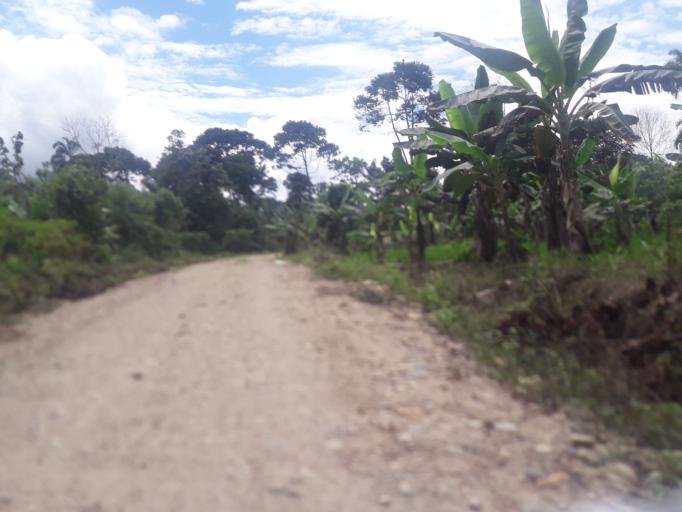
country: EC
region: Napo
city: Tena
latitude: -0.9756
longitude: -77.8511
